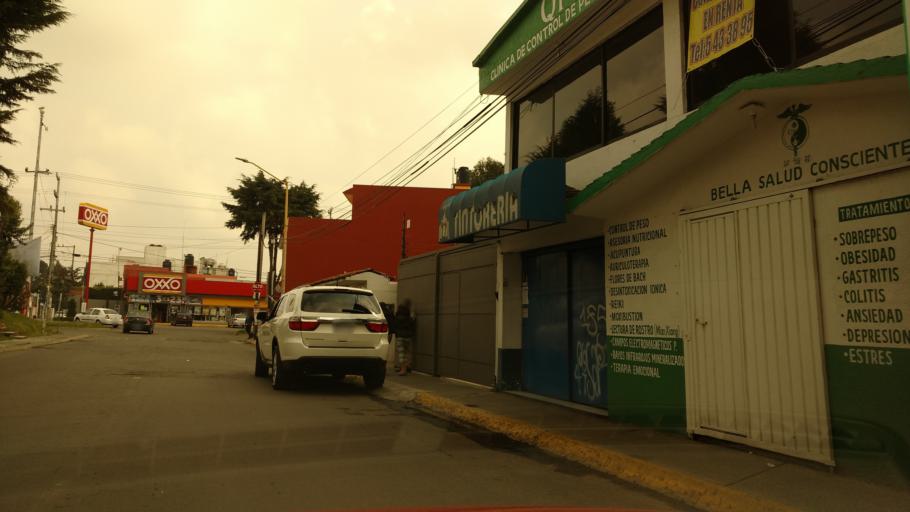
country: MX
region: Mexico
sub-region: Metepec
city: San Jorge Pueblo Nuevo
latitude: 19.2597
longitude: -99.6352
